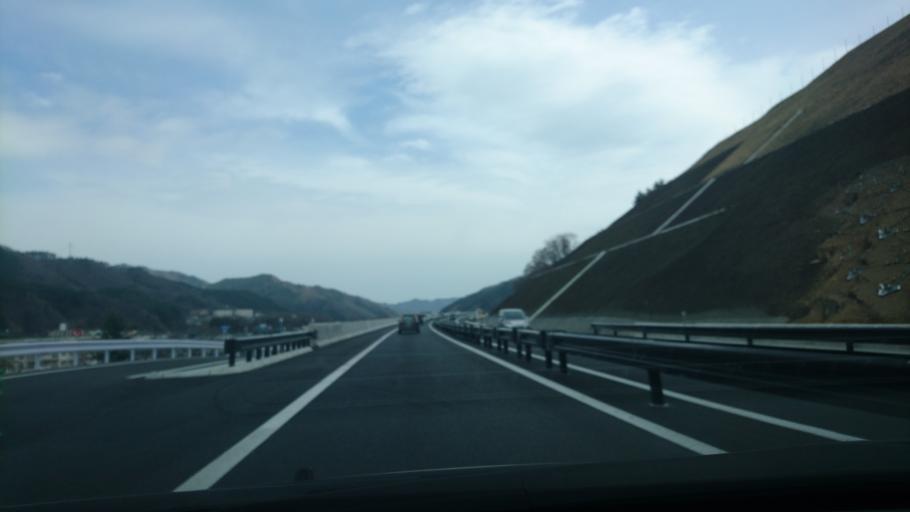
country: JP
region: Iwate
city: Kamaishi
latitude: 39.2535
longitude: 141.8167
